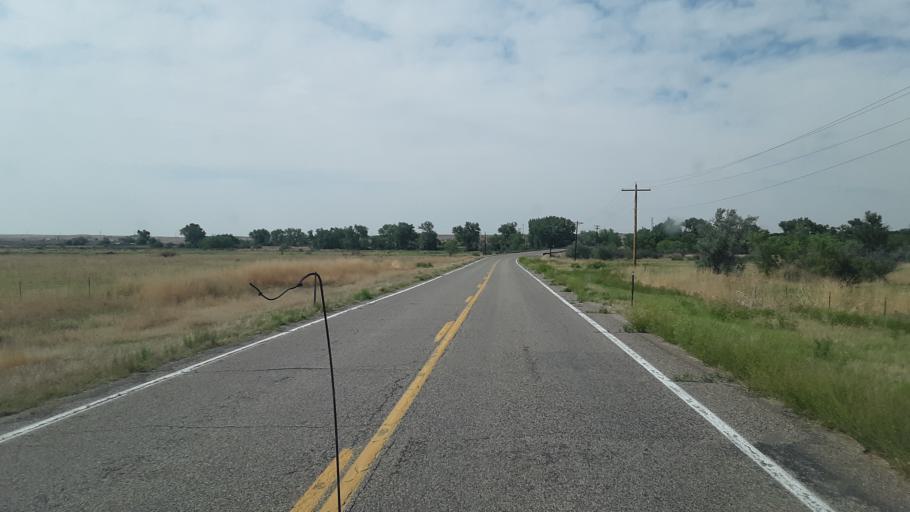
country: US
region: Colorado
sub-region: Otero County
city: Fowler
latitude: 38.2404
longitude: -104.2610
